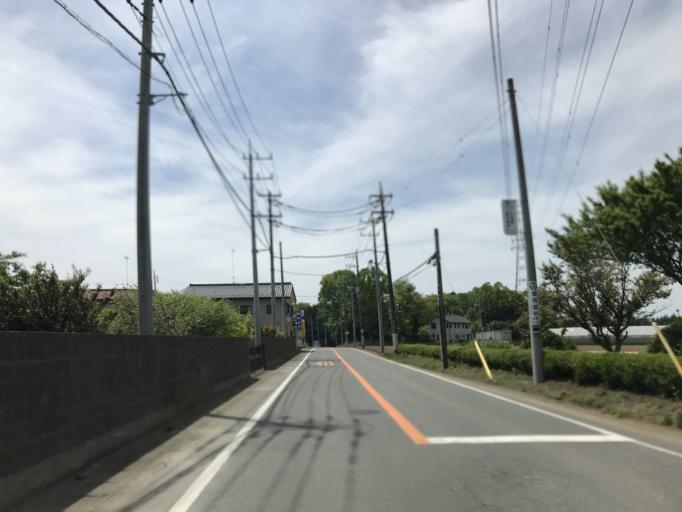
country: JP
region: Ibaraki
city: Mitsukaido
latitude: 35.9877
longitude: 139.9548
